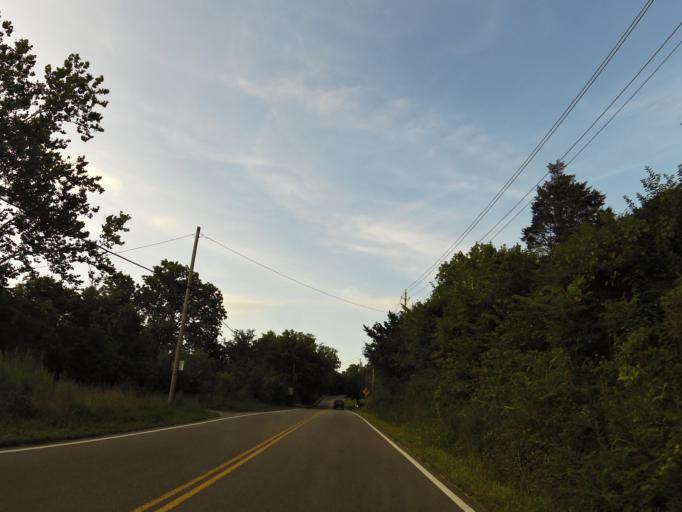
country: US
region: Tennessee
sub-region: Cocke County
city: Newport
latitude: 35.9611
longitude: -83.2751
